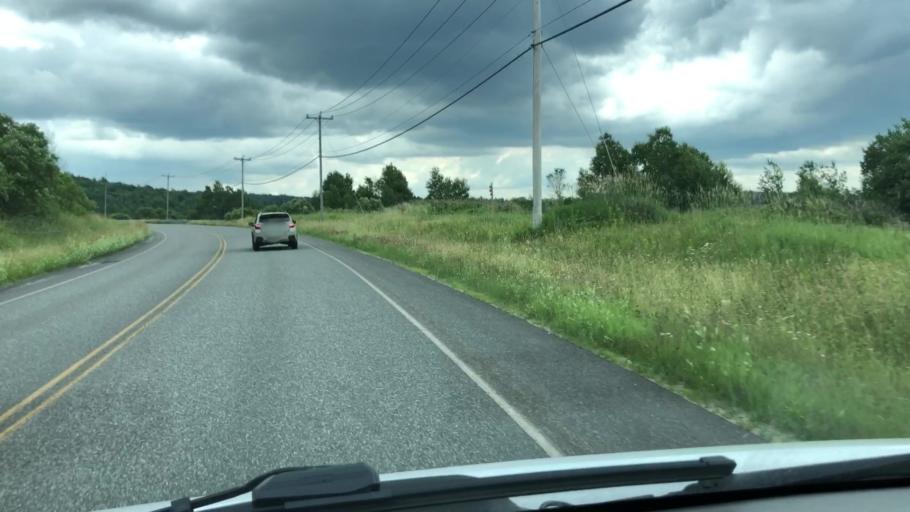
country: US
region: Massachusetts
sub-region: Berkshire County
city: Hinsdale
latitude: 42.5256
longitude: -73.0597
